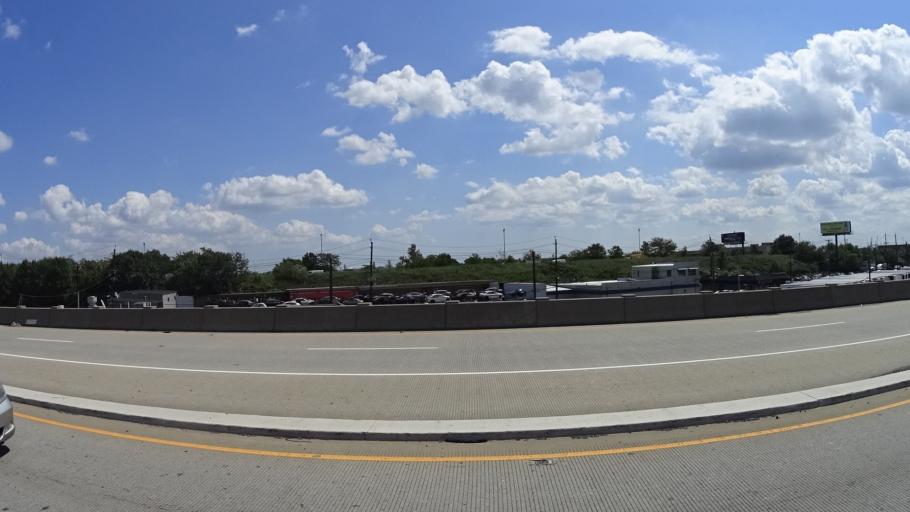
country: US
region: New Jersey
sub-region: Essex County
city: Newark
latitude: 40.7205
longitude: -74.1507
